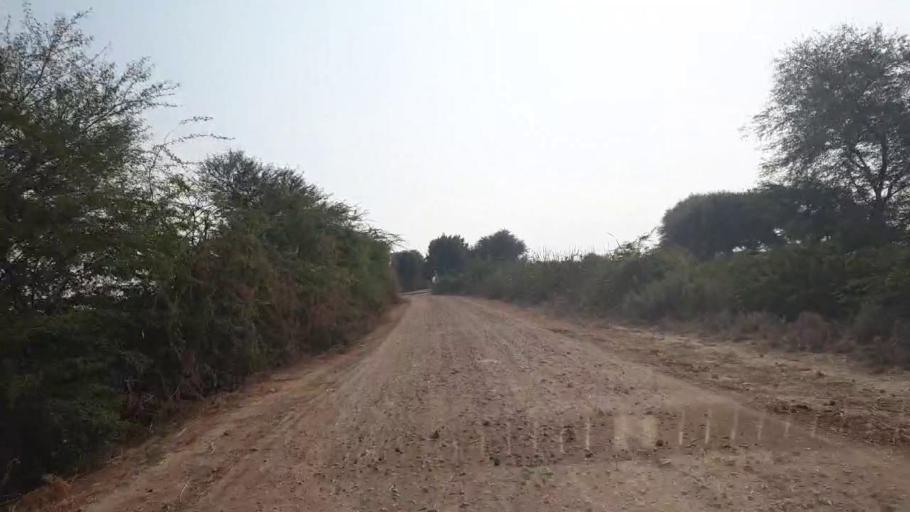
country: PK
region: Sindh
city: Matli
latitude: 24.9224
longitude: 68.6531
